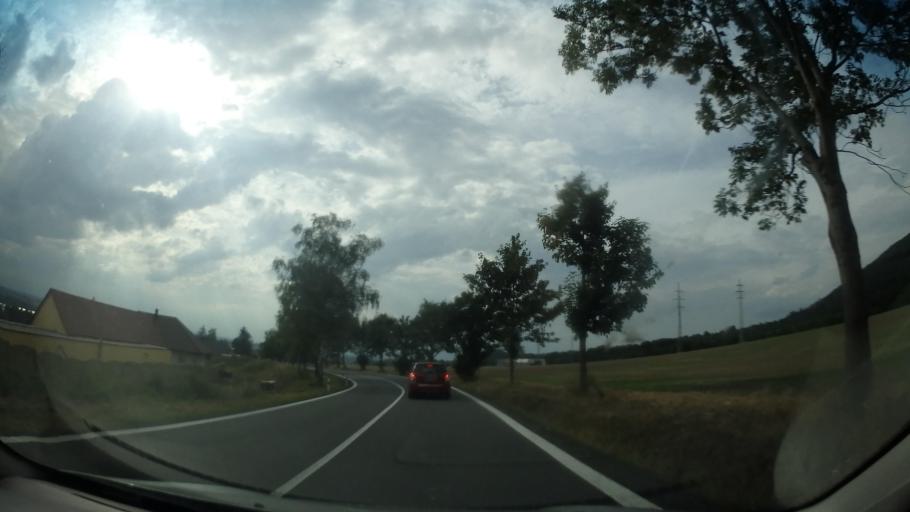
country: CZ
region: Pardubicky
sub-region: Okres Chrudim
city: Tremosnice
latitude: 49.8757
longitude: 15.5784
